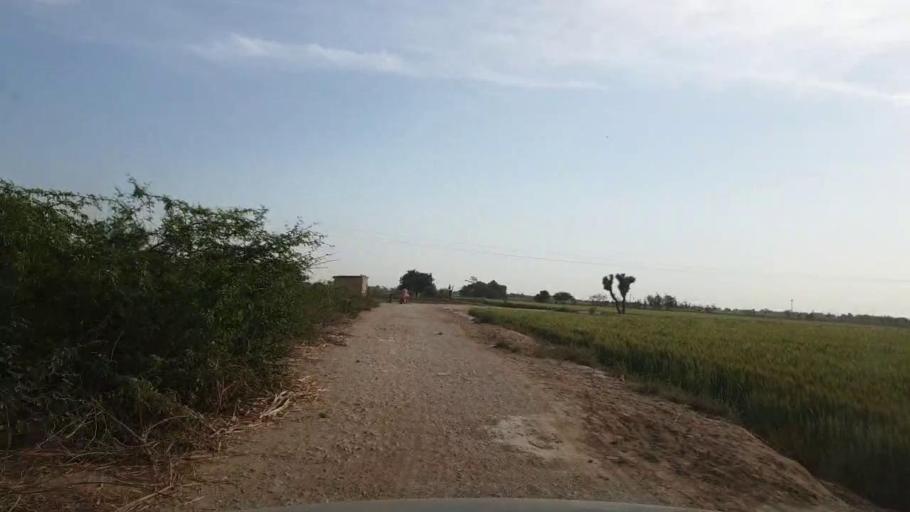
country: PK
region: Sindh
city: Kunri
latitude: 25.1479
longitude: 69.5072
